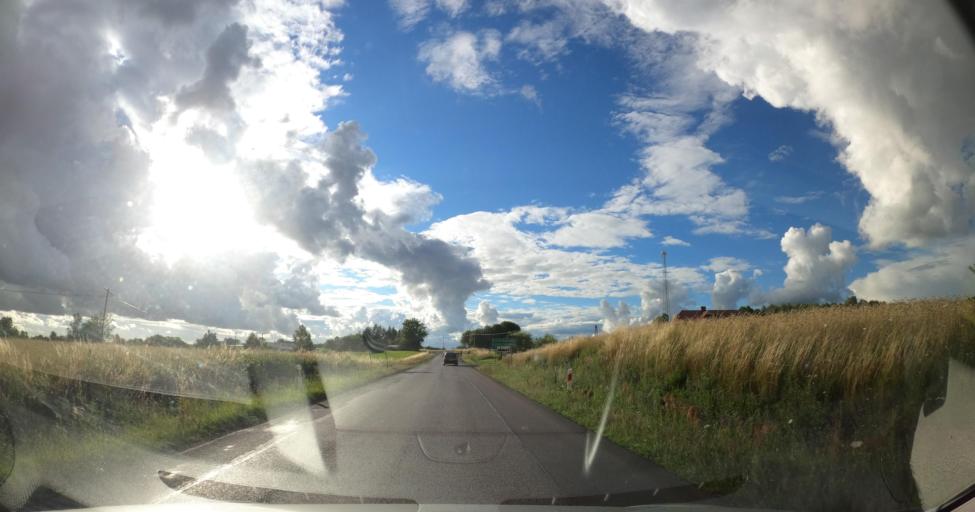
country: PL
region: Pomeranian Voivodeship
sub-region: Powiat bytowski
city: Czarna Dabrowka
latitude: 54.3527
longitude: 17.5759
